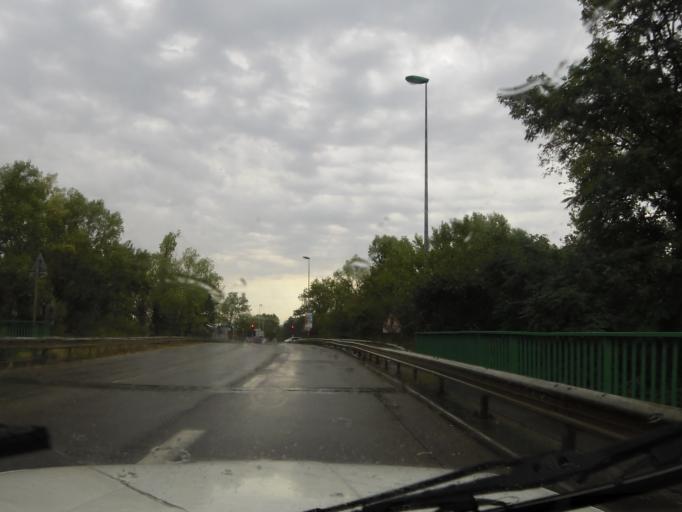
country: FR
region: Rhone-Alpes
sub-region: Departement du Rhone
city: Bron
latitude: 45.7213
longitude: 4.9337
